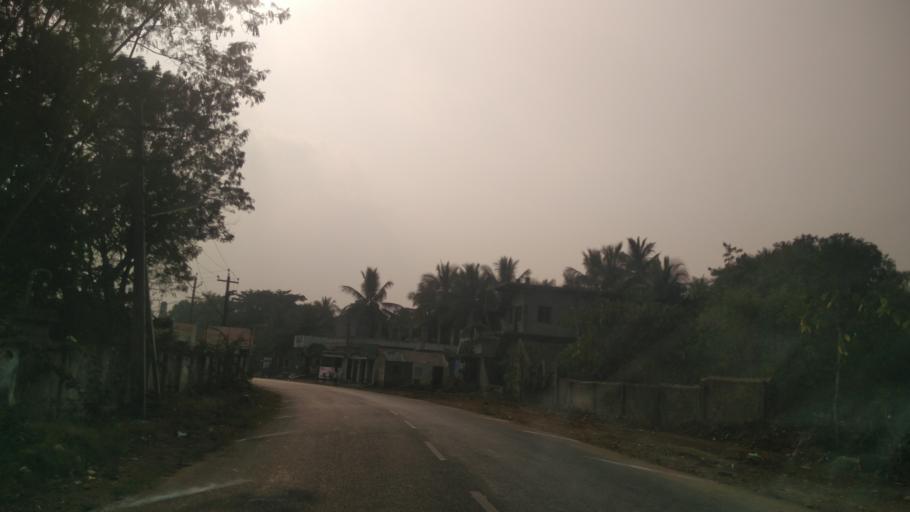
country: IN
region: Andhra Pradesh
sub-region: East Godavari
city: Rajahmundry
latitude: 16.9554
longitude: 81.7921
